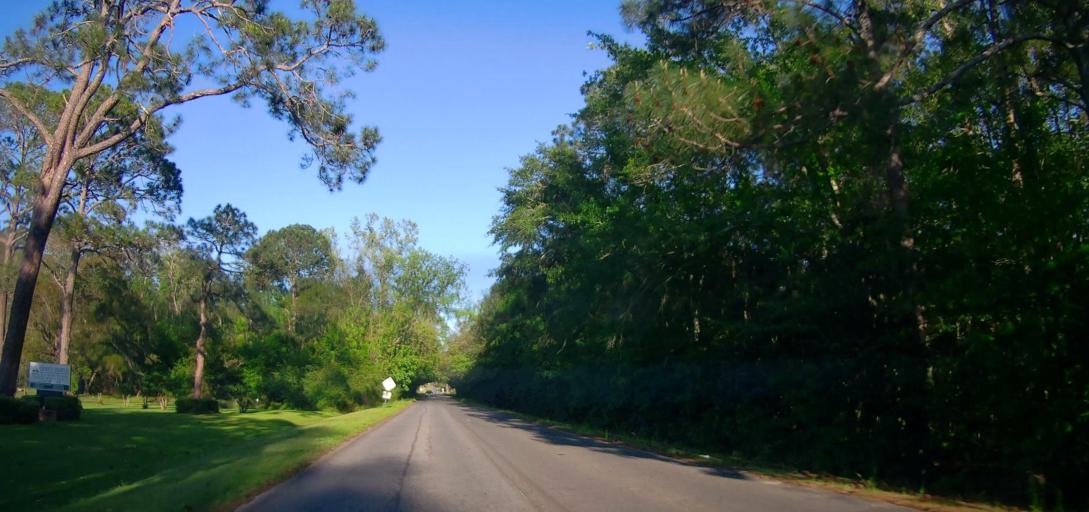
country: US
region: Georgia
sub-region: Ben Hill County
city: Fitzgerald
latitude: 31.7070
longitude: -83.2421
